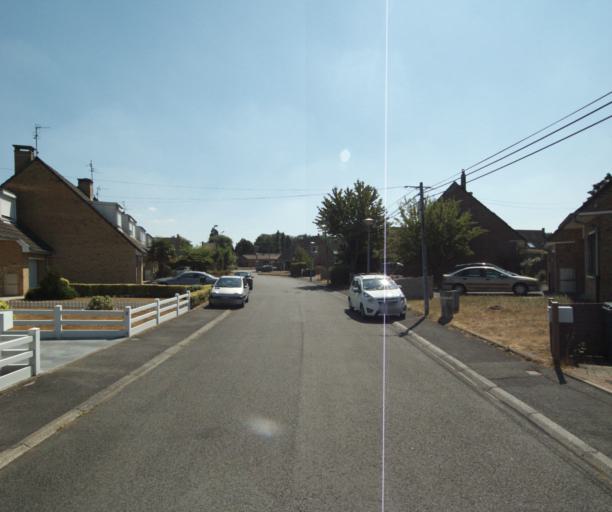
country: FR
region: Nord-Pas-de-Calais
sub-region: Departement du Nord
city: Halluin
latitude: 50.7785
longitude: 3.1102
